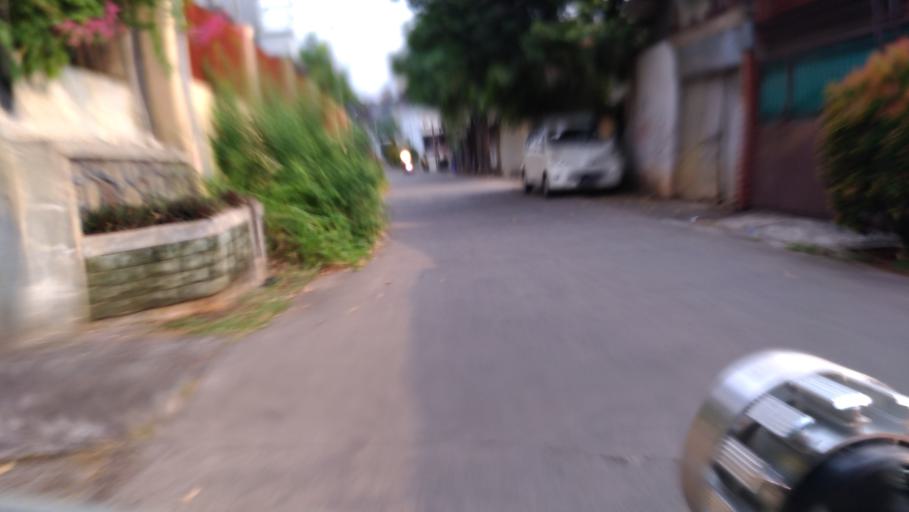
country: ID
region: West Java
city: Depok
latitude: -6.3616
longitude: 106.8662
